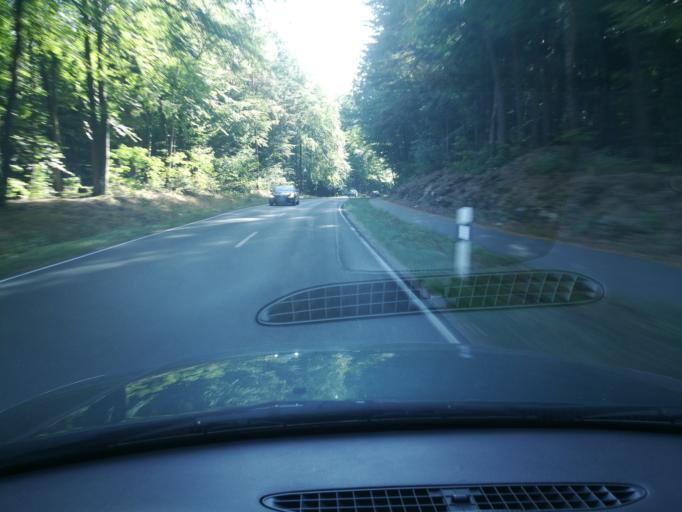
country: DE
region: Bavaria
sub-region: Regierungsbezirk Mittelfranken
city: Kalchreuth
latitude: 49.5491
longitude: 11.1106
